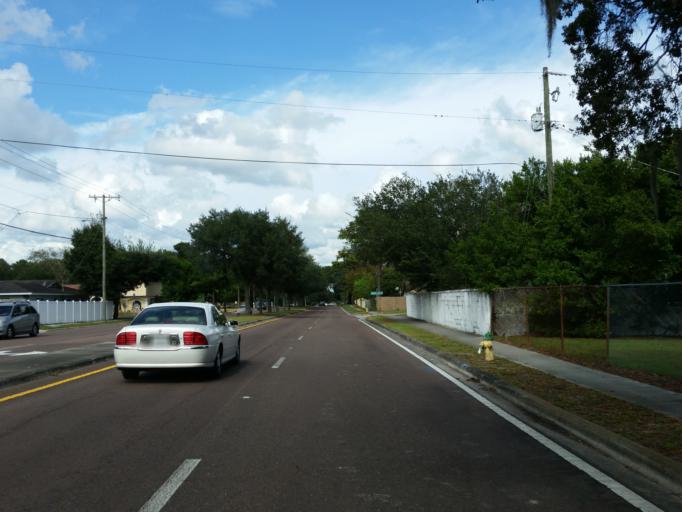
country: US
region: Florida
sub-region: Hillsborough County
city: Brandon
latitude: 27.9108
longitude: -82.2939
